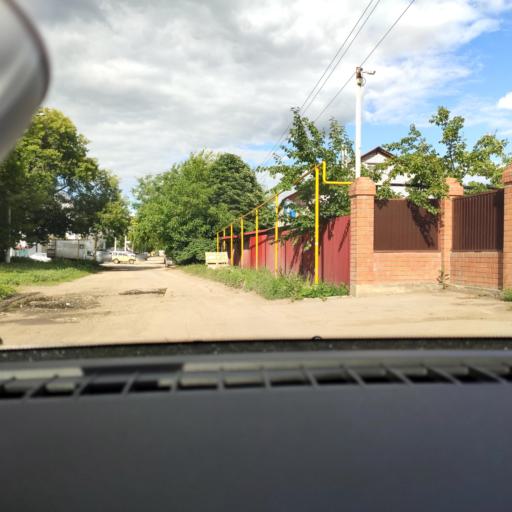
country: RU
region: Samara
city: Samara
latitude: 53.1774
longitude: 50.1960
